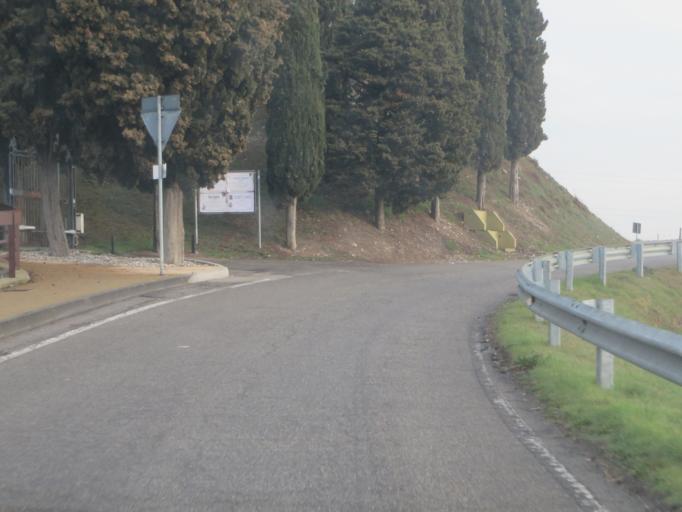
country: IT
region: Veneto
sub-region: Provincia di Verona
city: Sona
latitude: 45.4577
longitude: 10.8194
